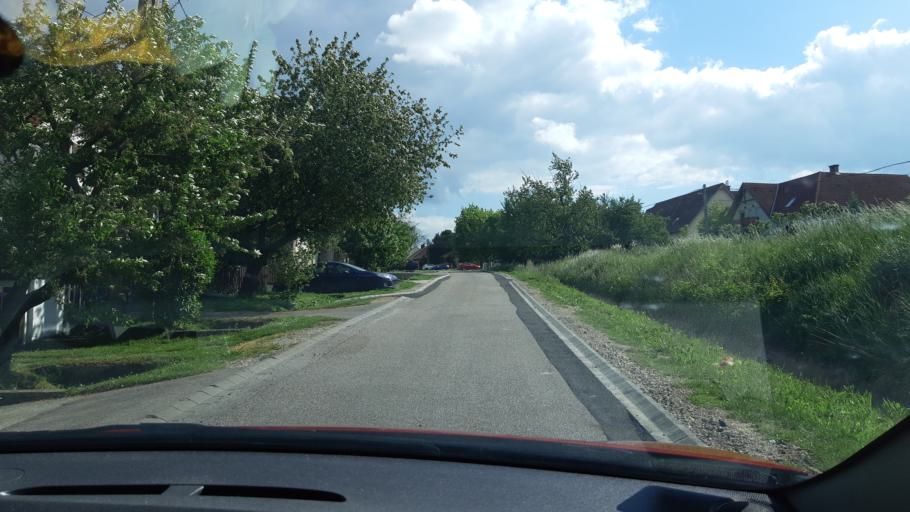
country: HU
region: Somogy
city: Kaposvar
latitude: 46.3603
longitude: 17.7622
